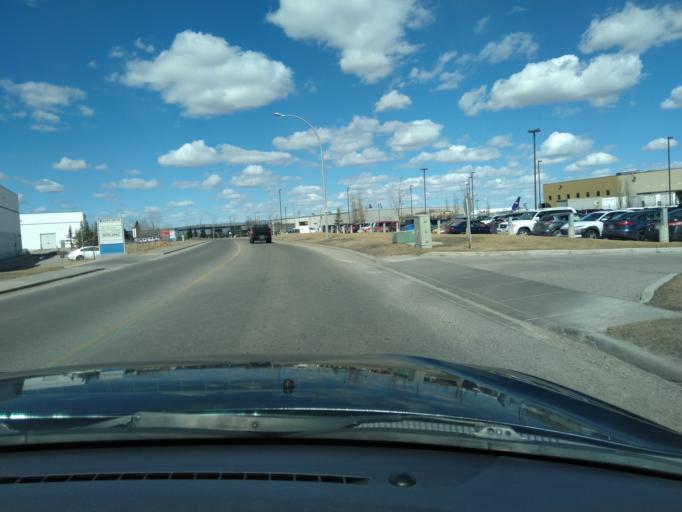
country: CA
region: Alberta
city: Calgary
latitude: 51.1172
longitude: -114.0303
